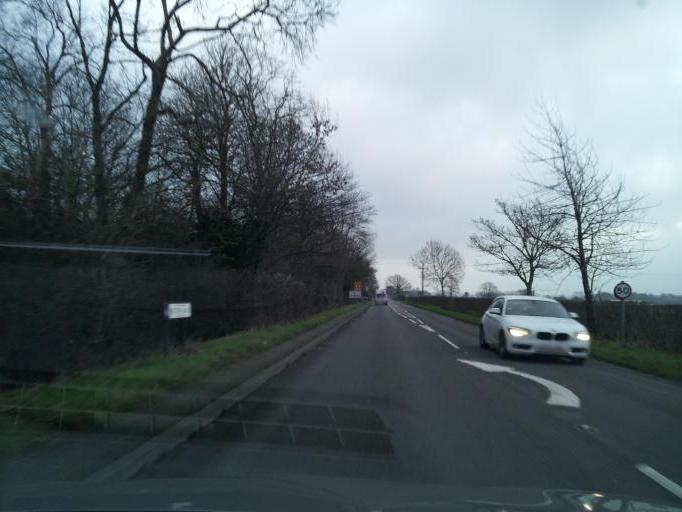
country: GB
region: England
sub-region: Derbyshire
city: Etwall
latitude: 52.8600
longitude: -1.6042
